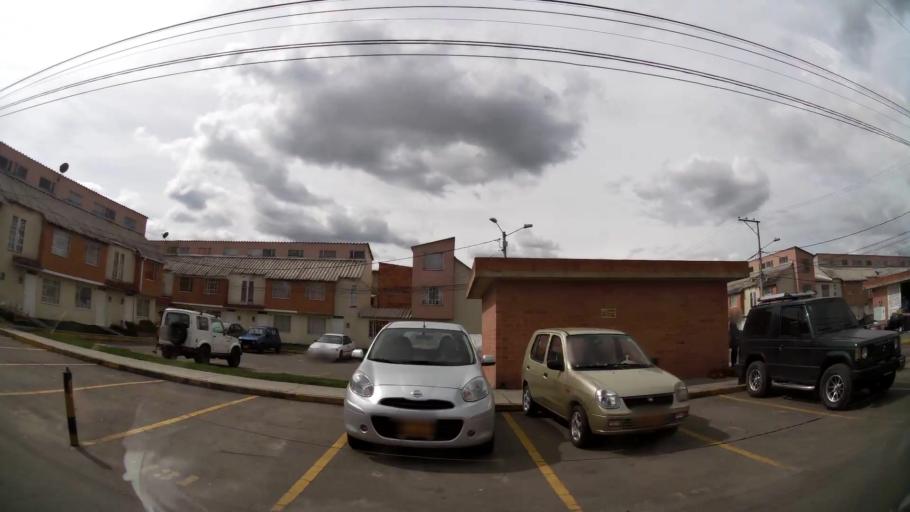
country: CO
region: Cundinamarca
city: Funza
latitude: 4.7106
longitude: -74.2009
